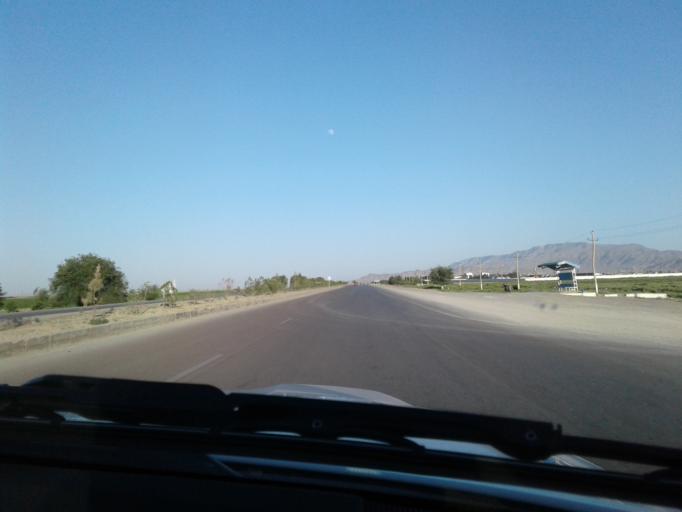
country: TM
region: Ahal
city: Baharly
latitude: 38.3278
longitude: 57.5844
